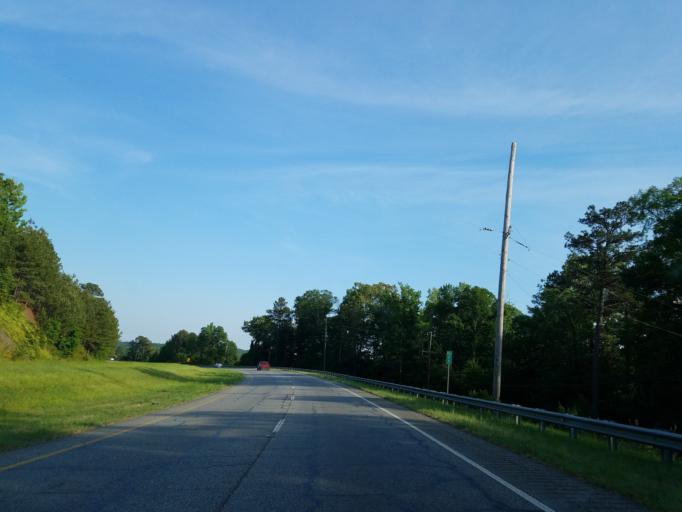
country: US
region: Georgia
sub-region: Chattooga County
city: Summerville
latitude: 34.4036
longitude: -85.2163
